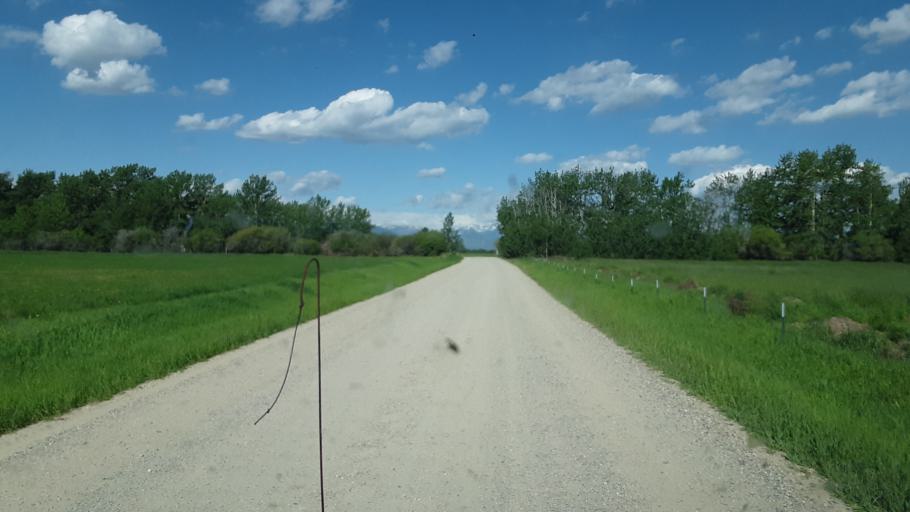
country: US
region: Montana
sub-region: Carbon County
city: Red Lodge
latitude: 45.2787
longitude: -109.1954
